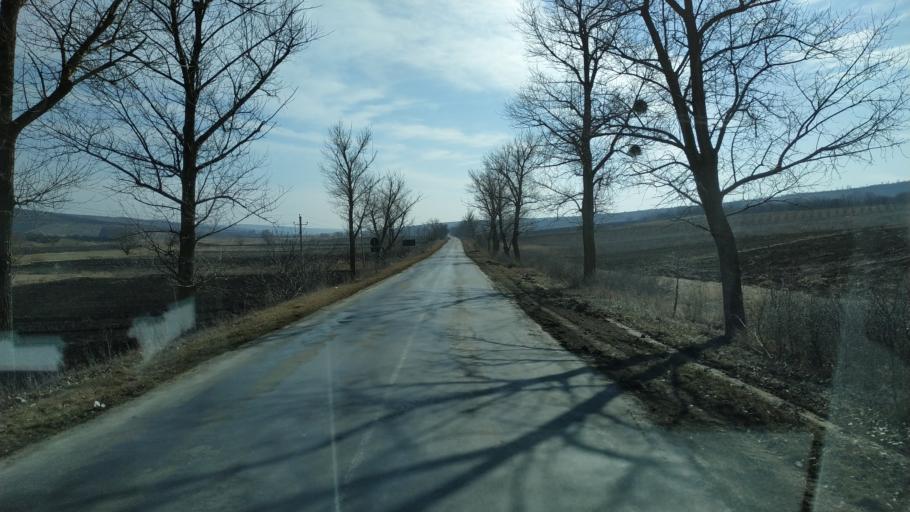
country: MD
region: Nisporeni
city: Nisporeni
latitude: 47.1190
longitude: 28.1217
